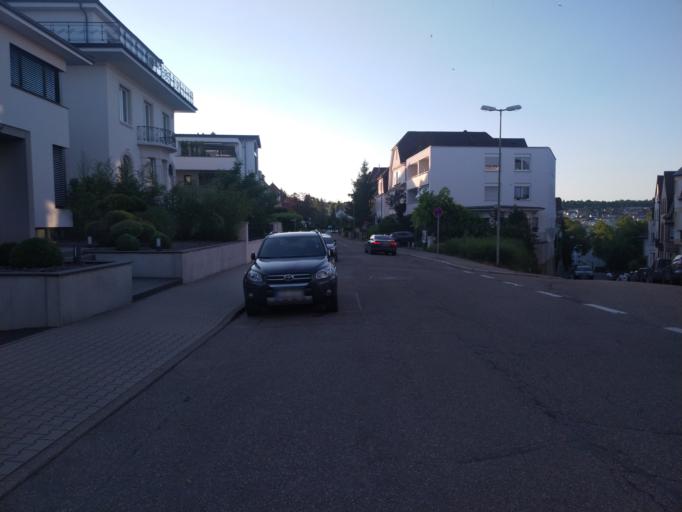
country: DE
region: Baden-Wuerttemberg
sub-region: Karlsruhe Region
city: Pforzheim
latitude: 48.8807
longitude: 8.6944
